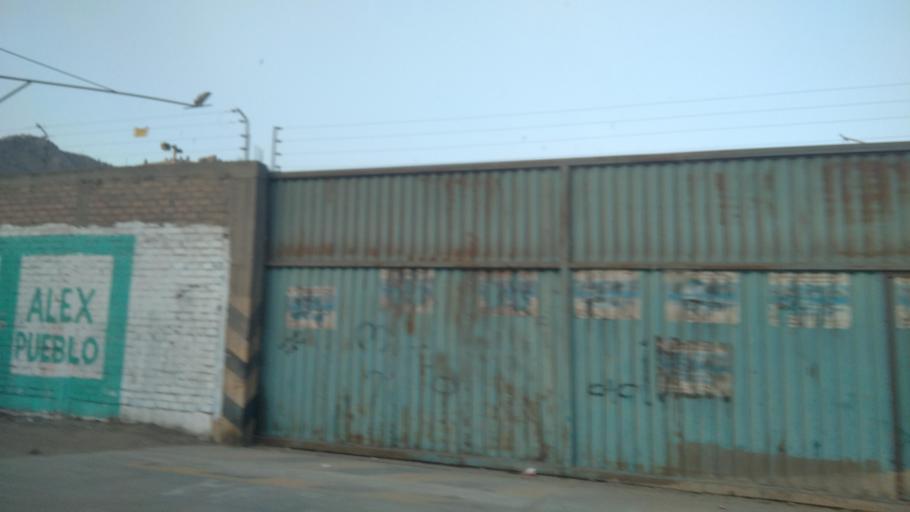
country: PE
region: Lima
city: Lima
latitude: -12.0140
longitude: -76.9944
